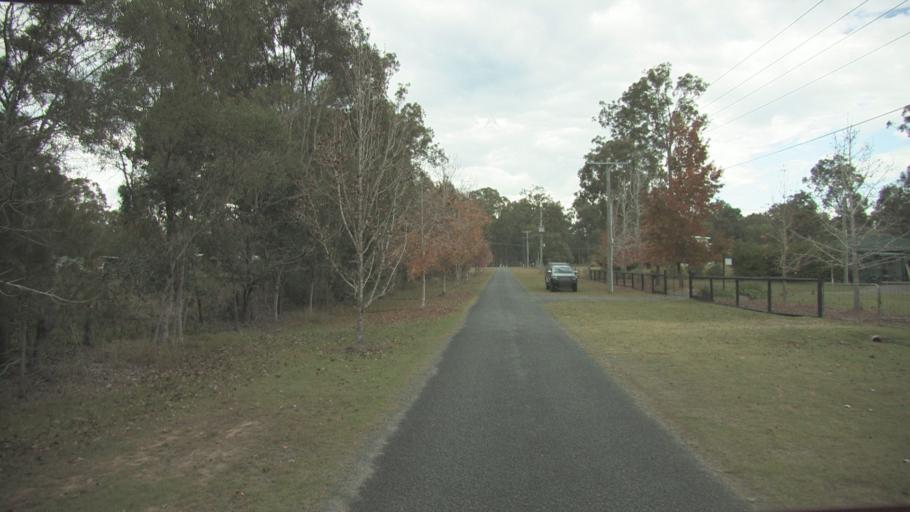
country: AU
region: Queensland
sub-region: Logan
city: Chambers Flat
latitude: -27.7820
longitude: 153.1126
